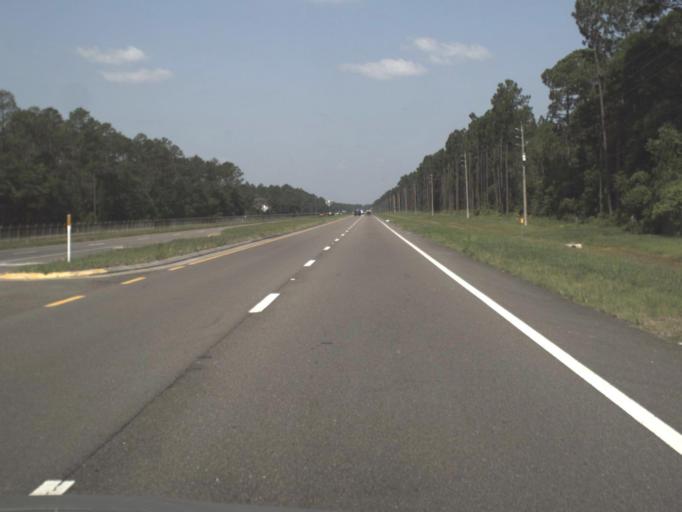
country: US
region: Florida
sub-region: Duval County
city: Baldwin
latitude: 30.2467
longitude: -81.8582
